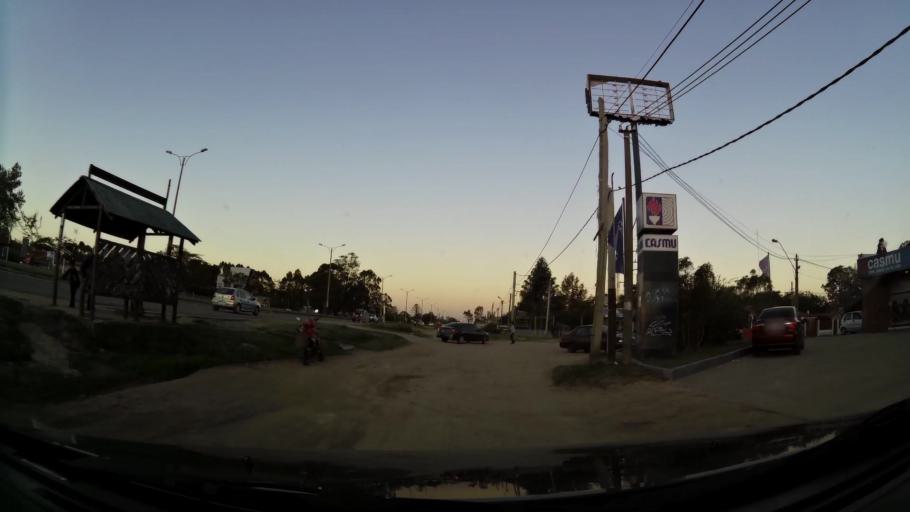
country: UY
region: Canelones
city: Colonia Nicolich
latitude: -34.8244
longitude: -55.9623
